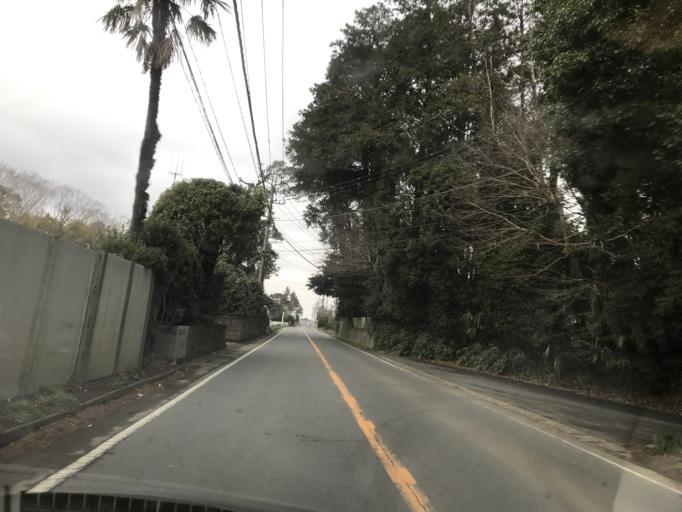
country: JP
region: Chiba
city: Sawara
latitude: 35.8452
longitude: 140.5083
